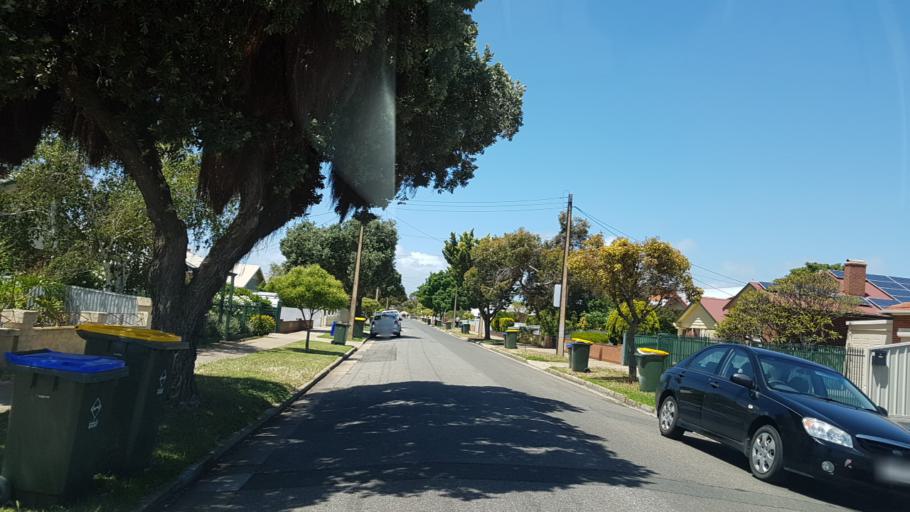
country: AU
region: South Australia
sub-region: Charles Sturt
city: Woodville West
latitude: -34.8817
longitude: 138.5260
